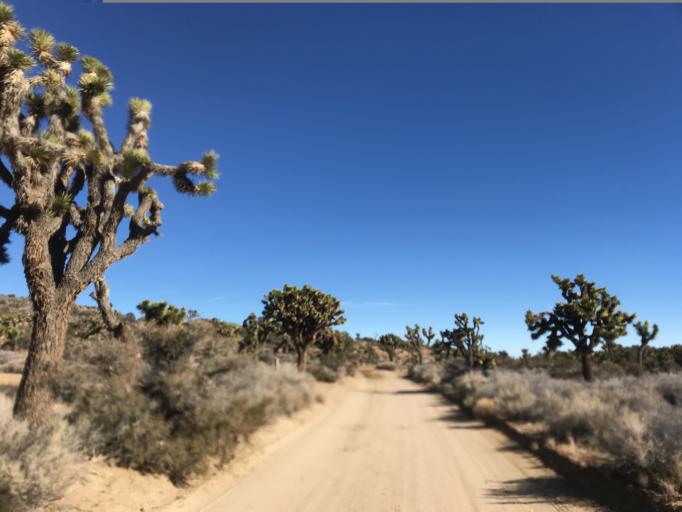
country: US
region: California
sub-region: San Bernardino County
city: Morongo Valley
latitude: 34.2267
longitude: -116.6363
